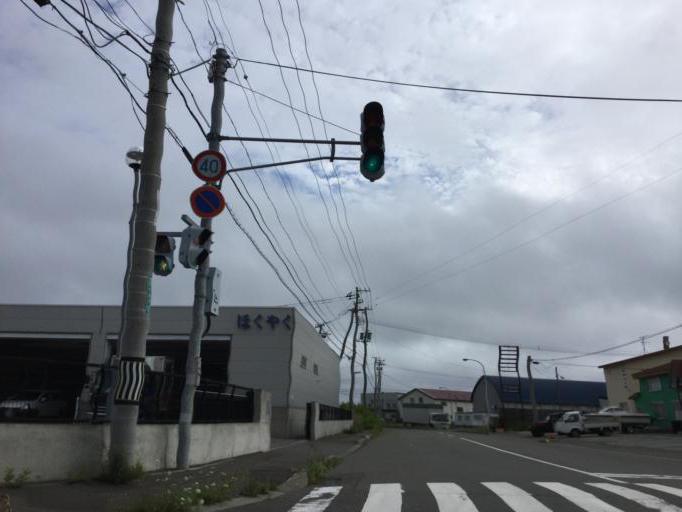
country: JP
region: Hokkaido
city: Wakkanai
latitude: 45.4004
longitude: 141.6896
